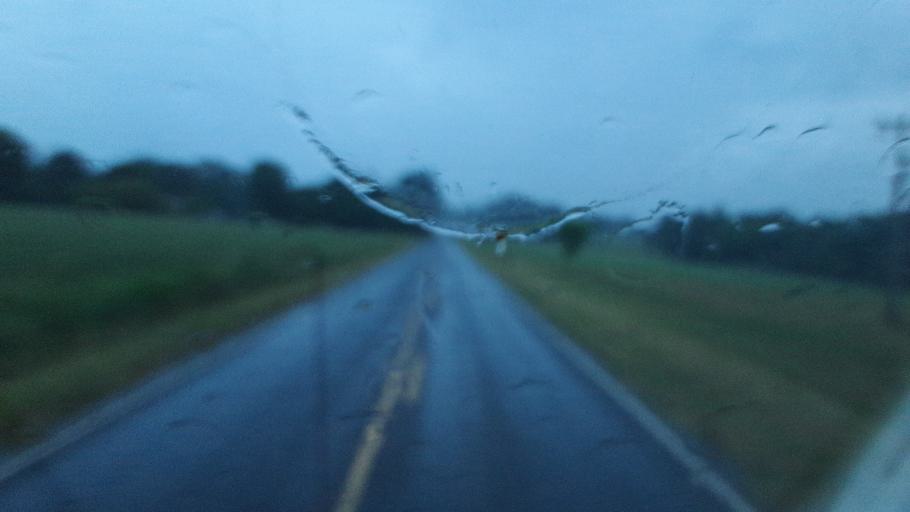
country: US
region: North Carolina
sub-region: Yadkin County
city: Jonesville
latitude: 36.0724
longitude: -80.8394
